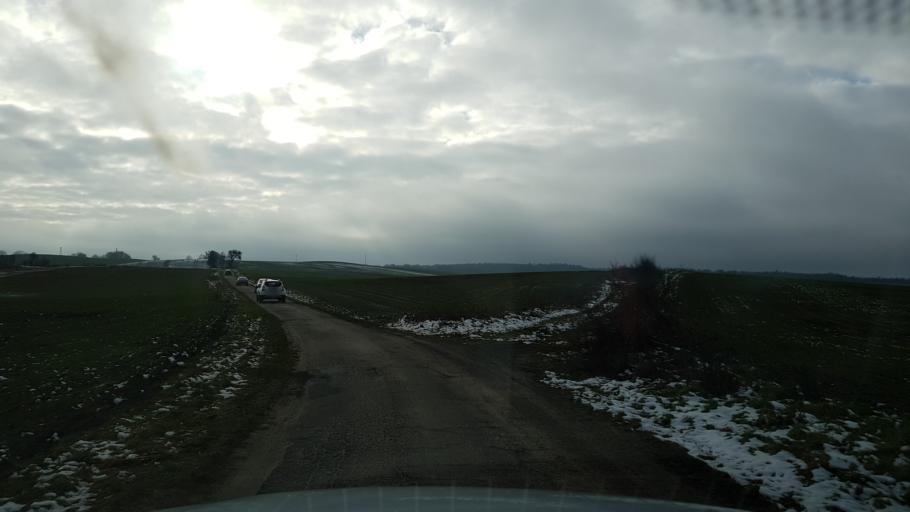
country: PL
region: West Pomeranian Voivodeship
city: Trzcinsko Zdroj
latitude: 52.9426
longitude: 14.7169
